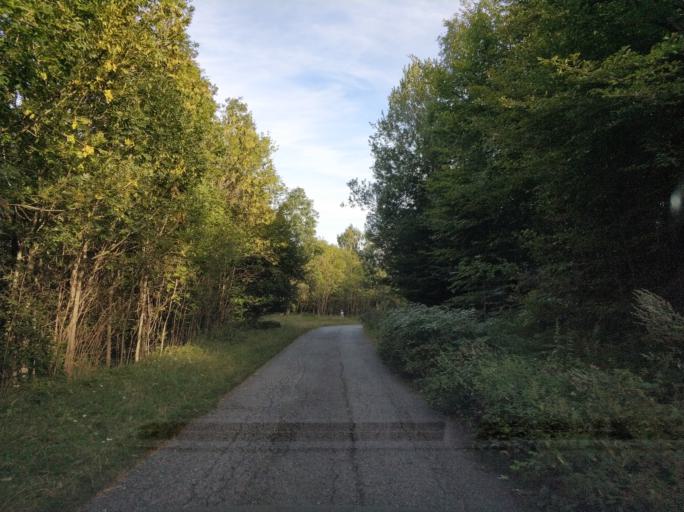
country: IT
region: Piedmont
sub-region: Provincia di Torino
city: Monastero di Lanzo
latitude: 45.3100
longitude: 7.4253
